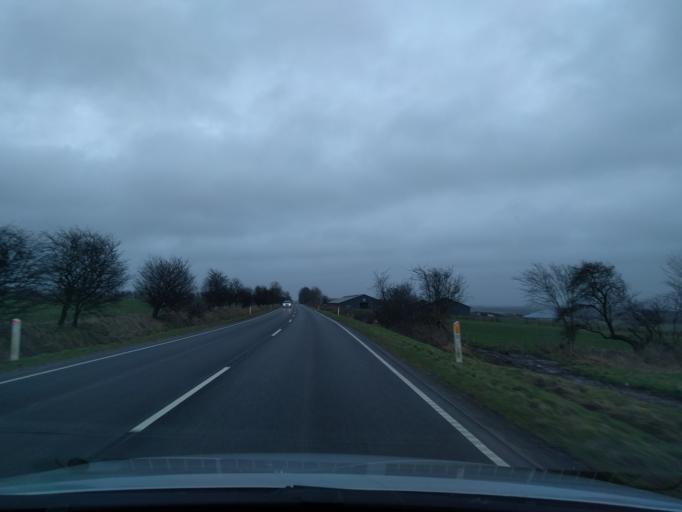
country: DK
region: South Denmark
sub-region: Tonder Kommune
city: Toftlund
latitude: 55.2515
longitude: 9.1611
